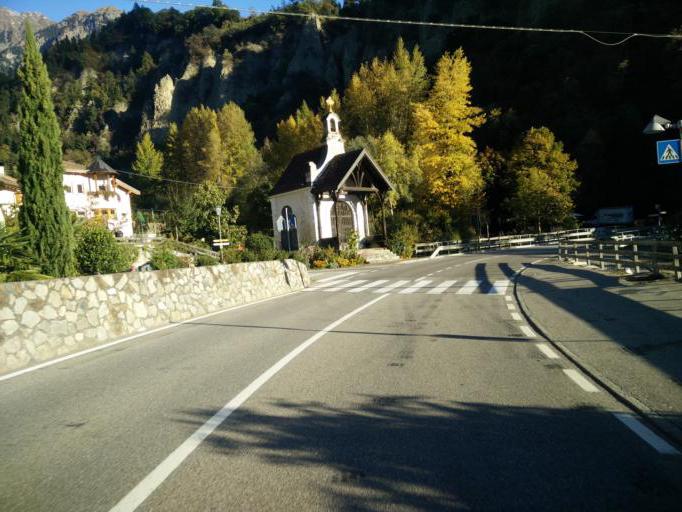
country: IT
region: Trentino-Alto Adige
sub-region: Bolzano
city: Caines
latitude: 46.6951
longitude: 11.1685
